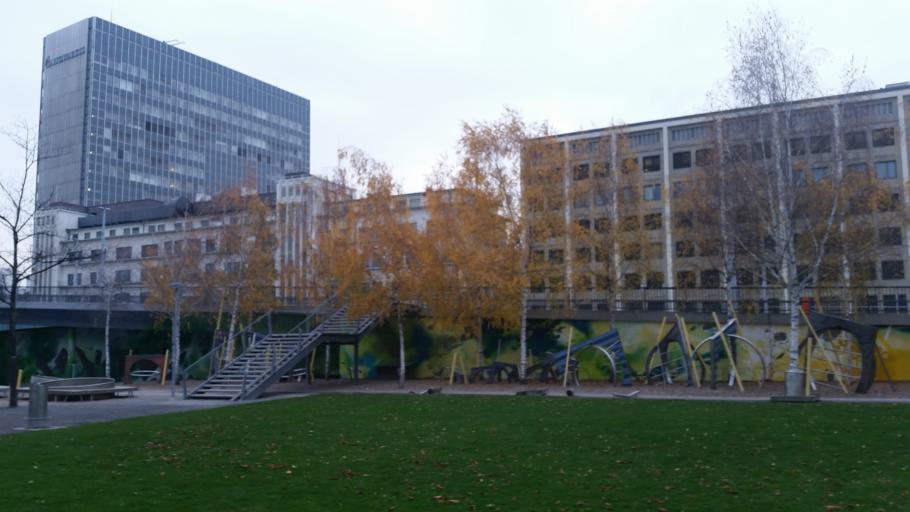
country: CH
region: Basel-City
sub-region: Basel-Stadt
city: Basel
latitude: 47.5701
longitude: 7.5890
